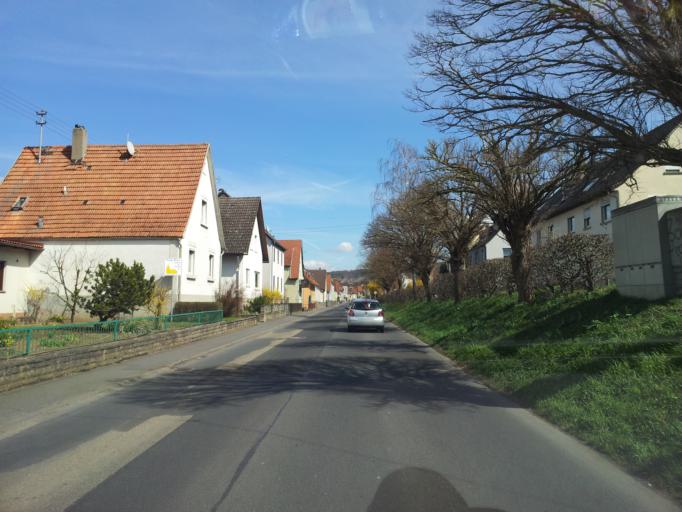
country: DE
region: Baden-Wuerttemberg
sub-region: Regierungsbezirk Stuttgart
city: Lauda-Konigshofen
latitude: 49.5783
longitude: 9.7107
